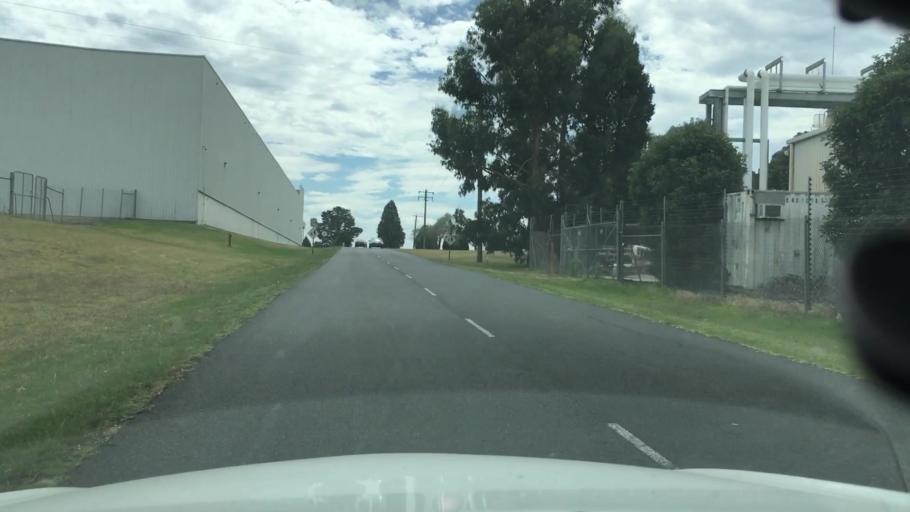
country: AU
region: Victoria
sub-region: Knox
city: Scoresby
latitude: -37.9039
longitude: 145.2265
